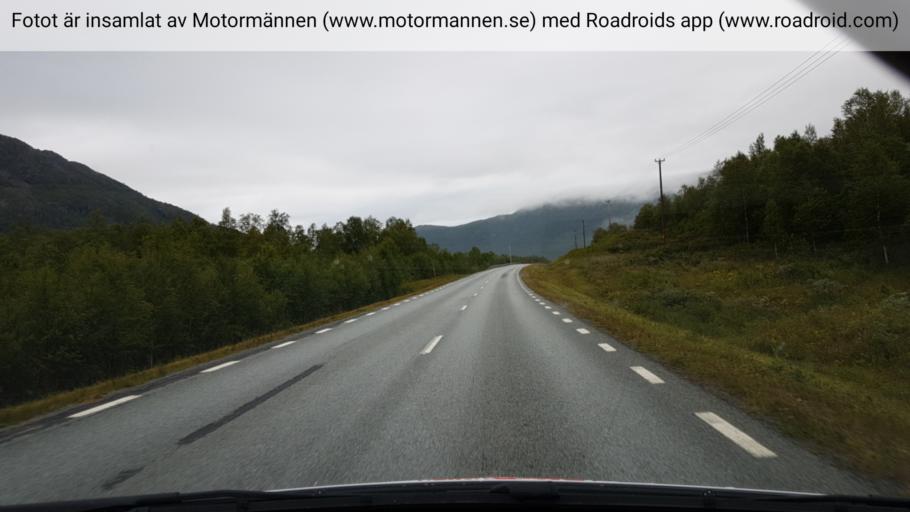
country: NO
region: Nordland
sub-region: Rana
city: Mo i Rana
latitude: 65.9239
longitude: 15.0075
